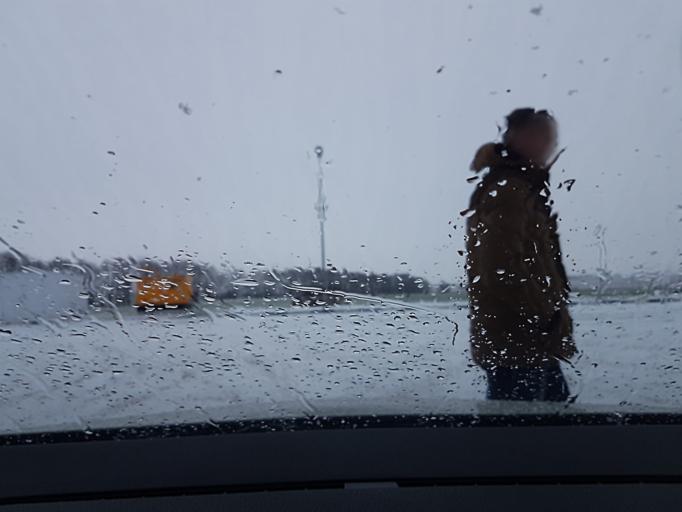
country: RU
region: Rjazan
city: Ryazhsk
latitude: 53.6562
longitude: 39.9835
